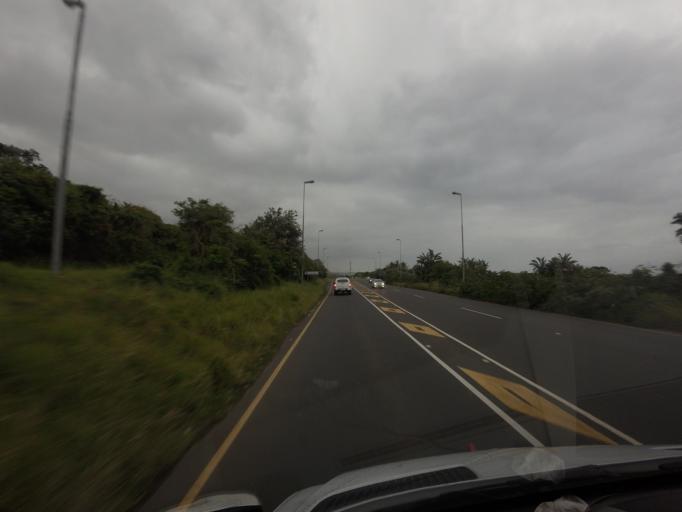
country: ZA
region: KwaZulu-Natal
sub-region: iLembe District Municipality
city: Ballitoville
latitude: -29.5987
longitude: 31.1657
